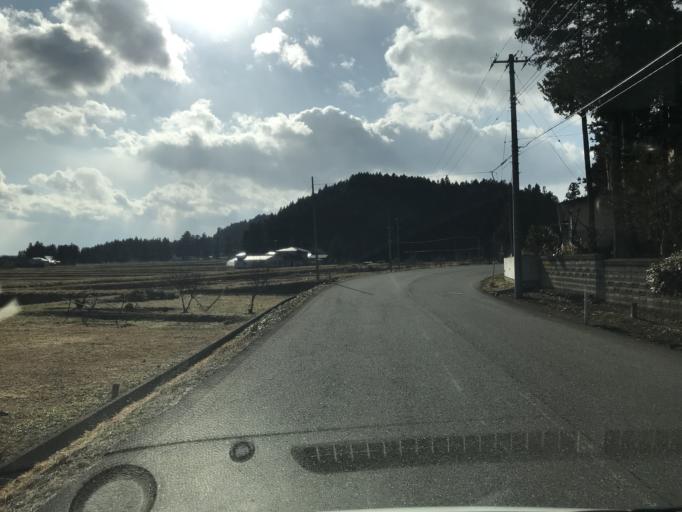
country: JP
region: Iwate
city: Mizusawa
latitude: 39.1437
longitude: 141.0349
